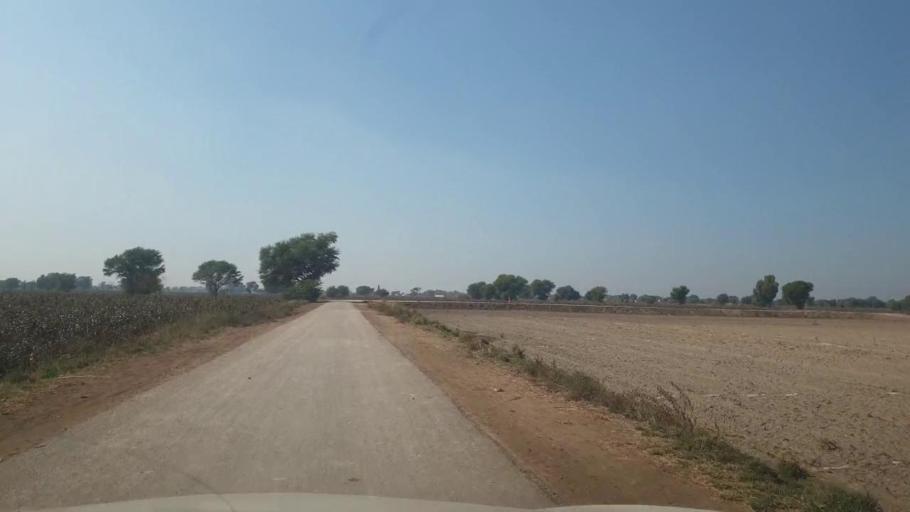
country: PK
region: Sindh
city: Bhan
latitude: 26.5685
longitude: 67.7125
